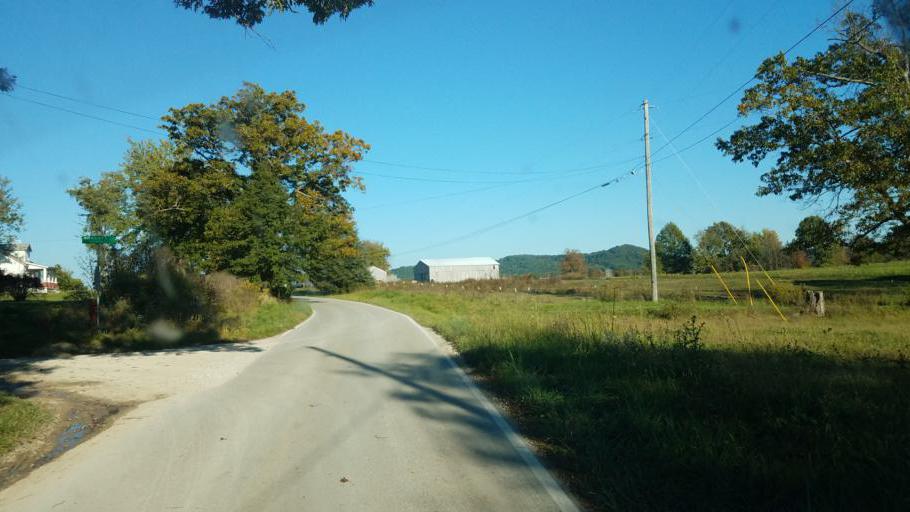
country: US
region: Kentucky
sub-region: Fleming County
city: Flemingsburg
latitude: 38.4913
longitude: -83.5871
